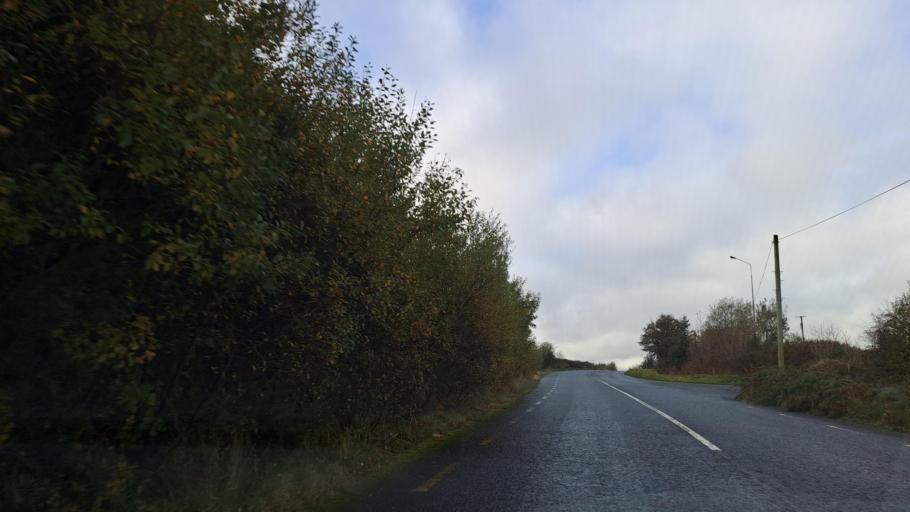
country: IE
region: Ulster
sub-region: An Cabhan
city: Bailieborough
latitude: 53.8909
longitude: -7.0218
